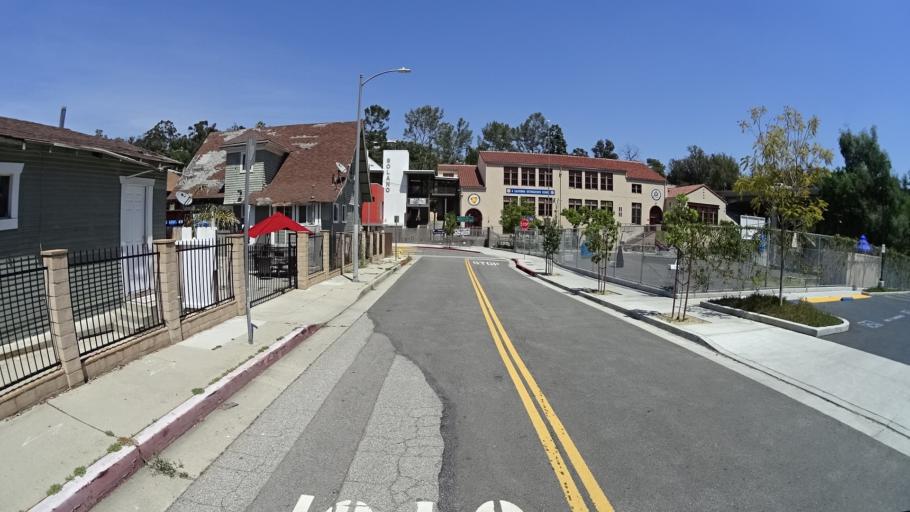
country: US
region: California
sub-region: Los Angeles County
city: Los Angeles
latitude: 34.0757
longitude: -118.2328
